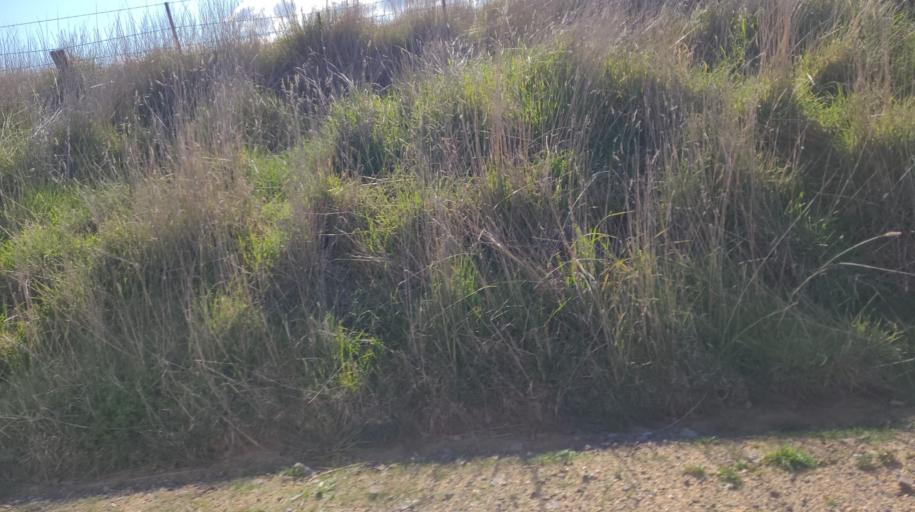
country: AU
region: New South Wales
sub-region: Blayney
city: Blayney
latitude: -33.4176
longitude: 149.3139
